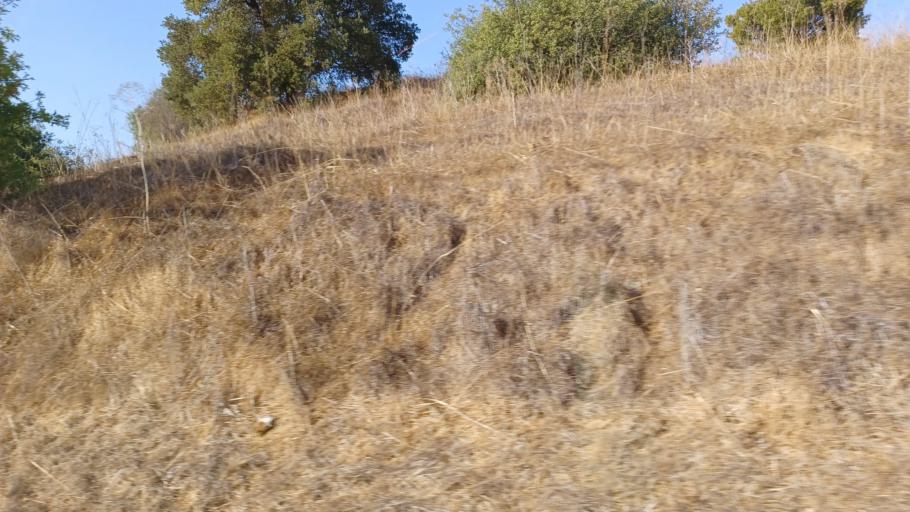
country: CY
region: Pafos
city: Polis
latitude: 34.9691
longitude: 32.4229
